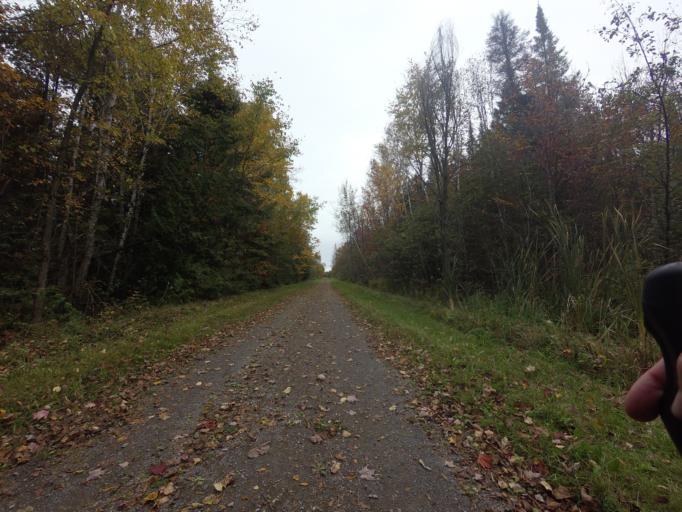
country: CA
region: Quebec
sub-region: Outaouais
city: Shawville
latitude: 45.6278
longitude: -76.5084
